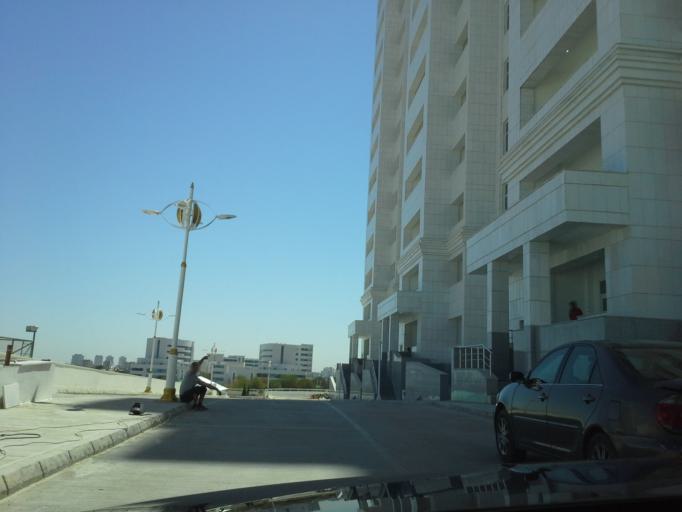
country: TM
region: Ahal
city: Ashgabat
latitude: 37.9419
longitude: 58.3543
